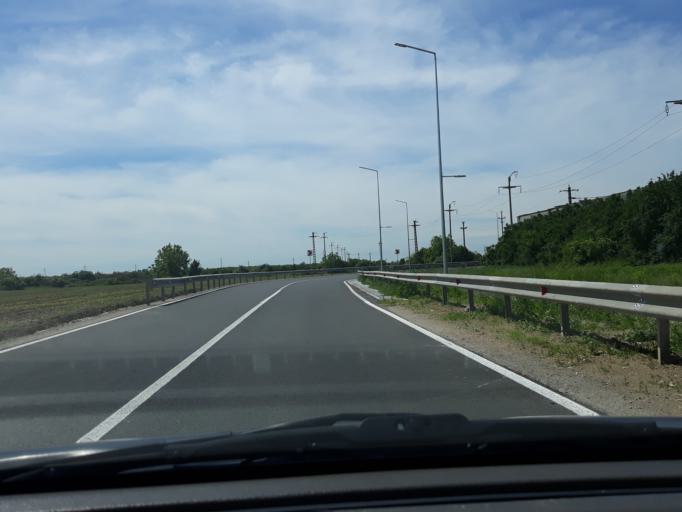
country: RO
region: Bihor
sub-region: Comuna Santandrei
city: Santandrei
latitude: 47.0677
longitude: 21.8899
